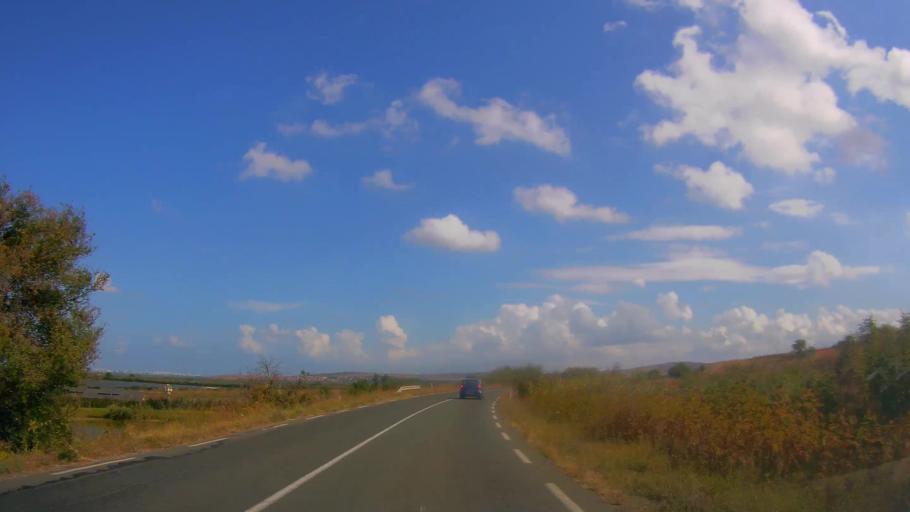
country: BG
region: Burgas
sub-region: Obshtina Kameno
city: Kameno
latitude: 42.4914
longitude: 27.3366
